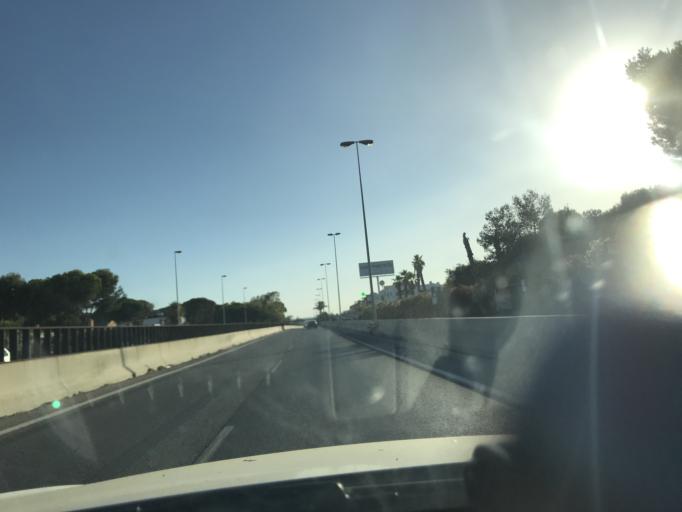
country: ES
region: Andalusia
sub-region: Provincia de Malaga
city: Benahavis
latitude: 36.4663
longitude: -5.0264
